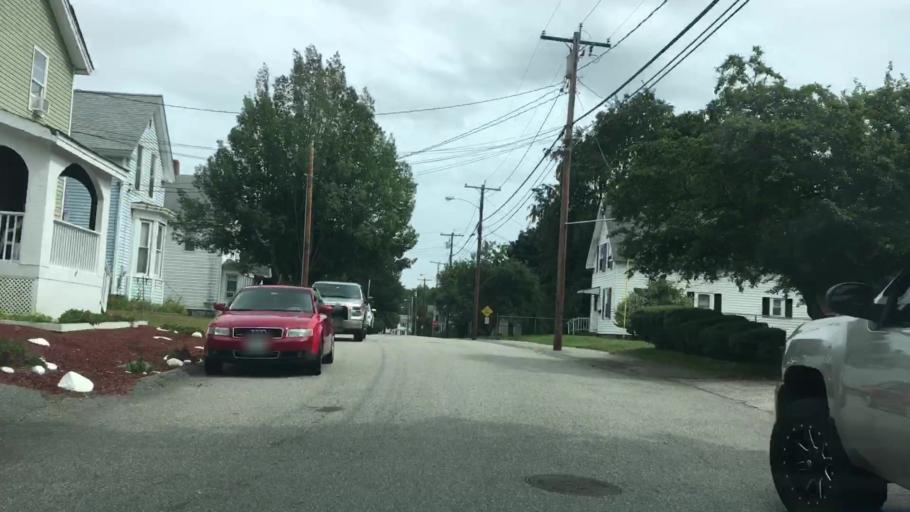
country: US
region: Maine
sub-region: Cumberland County
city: Westbrook
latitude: 43.6725
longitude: -70.3654
